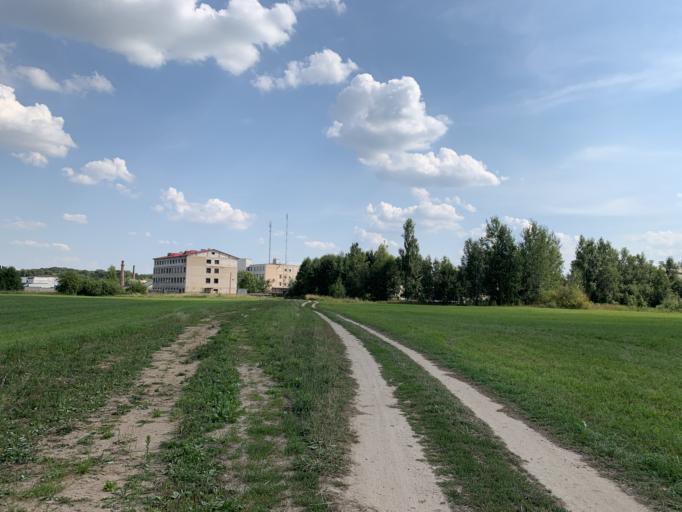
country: BY
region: Minsk
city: Nyasvizh
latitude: 53.2075
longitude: 26.6361
